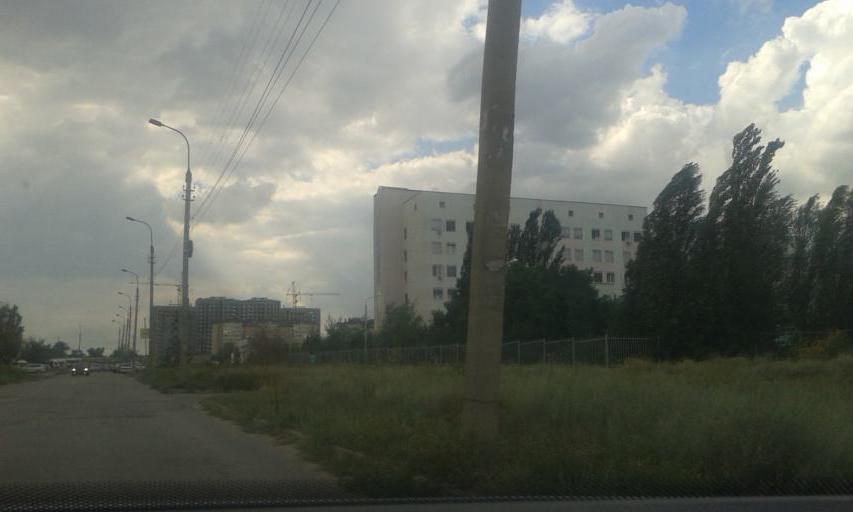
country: RU
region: Volgograd
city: Volgograd
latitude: 48.6416
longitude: 44.4185
